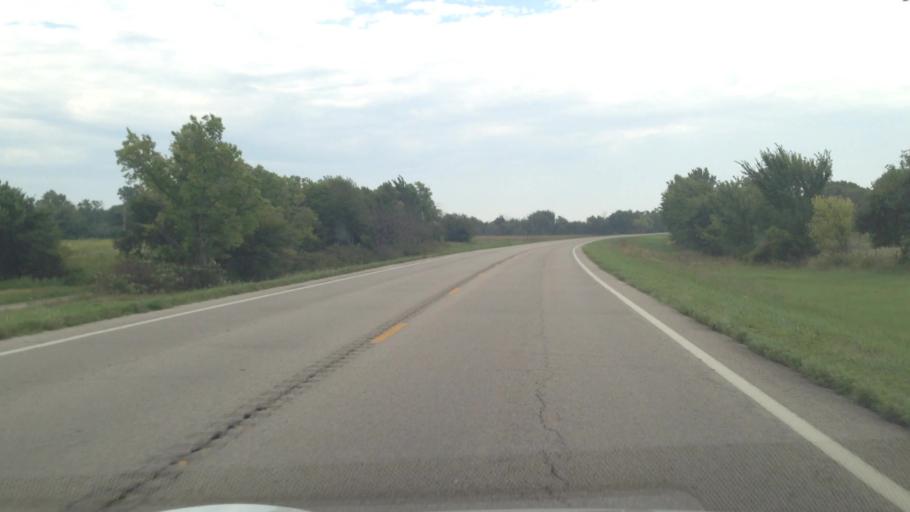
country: US
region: Kansas
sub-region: Bourbon County
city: Fort Scott
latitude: 37.8921
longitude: -95.0421
